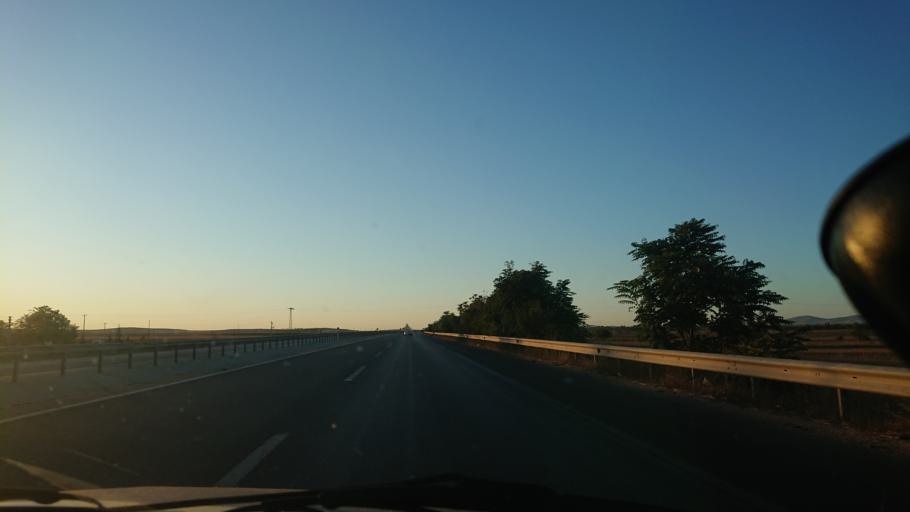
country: TR
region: Eskisehir
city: Mahmudiye
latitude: 39.5419
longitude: 30.9377
